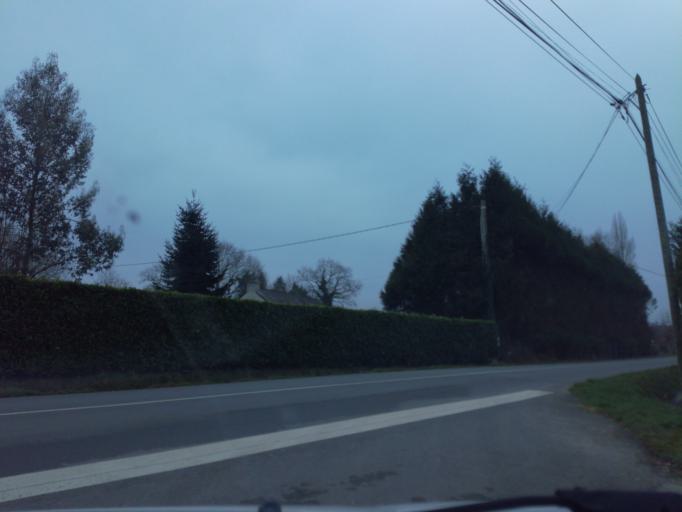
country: FR
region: Brittany
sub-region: Departement d'Ille-et-Vilaine
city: Gosne
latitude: 48.2606
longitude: -1.4504
